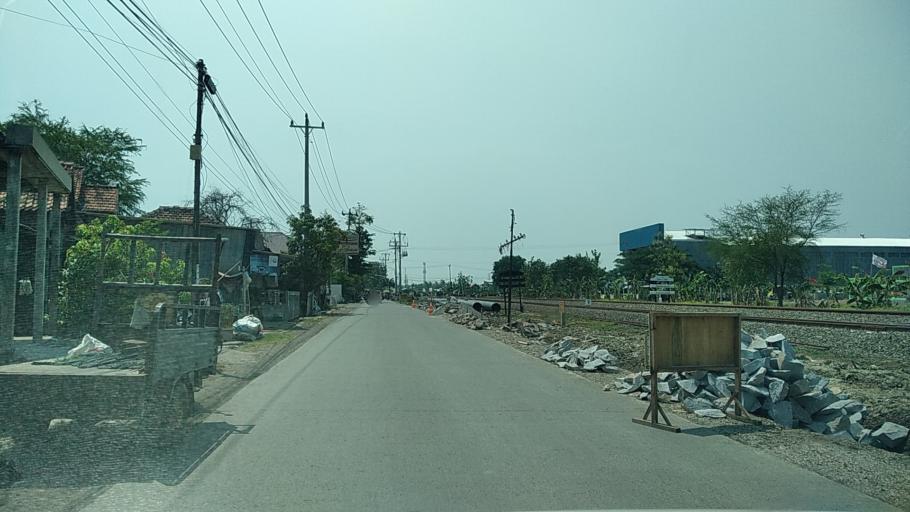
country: ID
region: Central Java
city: Semarang
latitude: -6.9714
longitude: 110.4612
